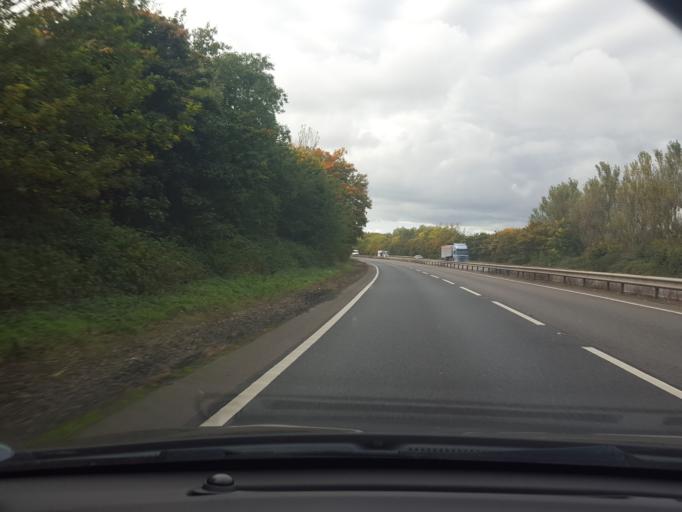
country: GB
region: England
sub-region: Suffolk
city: Thurston
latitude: 52.2372
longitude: 0.8348
